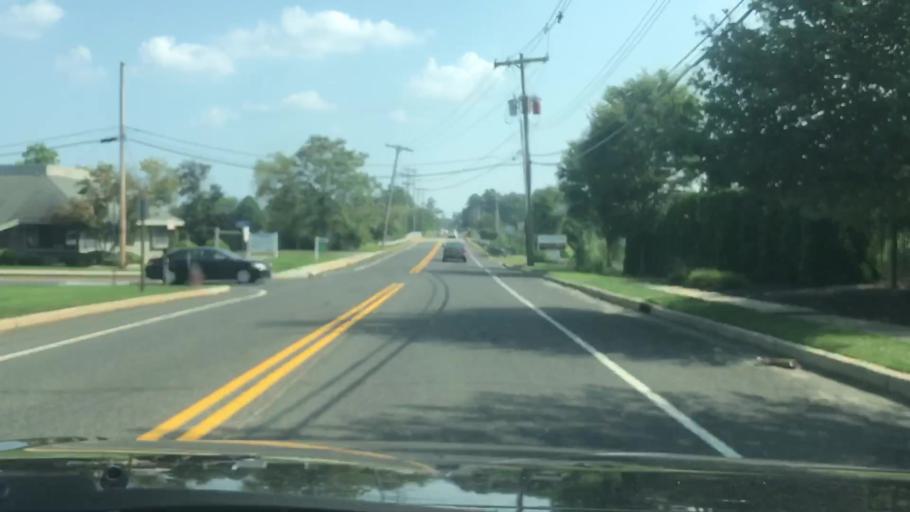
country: US
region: New Jersey
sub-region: Monmouth County
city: Little Silver
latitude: 40.3232
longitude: -74.0375
